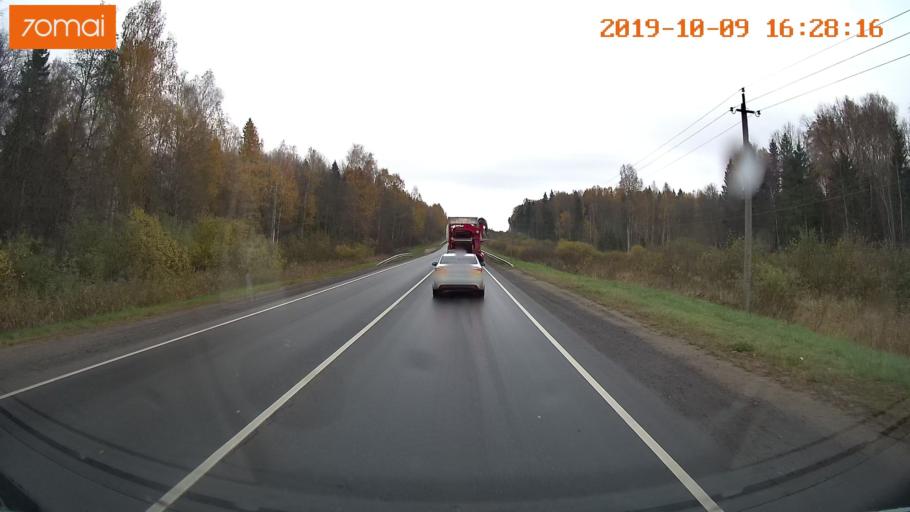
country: RU
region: Kostroma
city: Oktyabr'skiy
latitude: 57.6295
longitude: 40.9314
